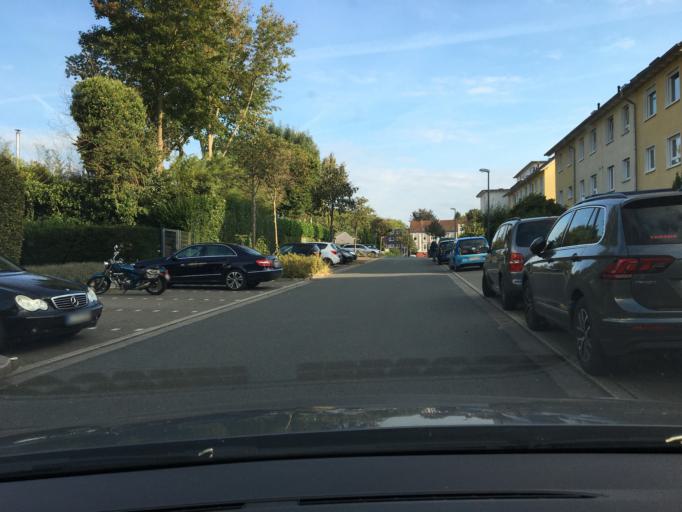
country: DE
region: North Rhine-Westphalia
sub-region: Regierungsbezirk Dusseldorf
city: Essen
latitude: 51.4514
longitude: 7.0681
